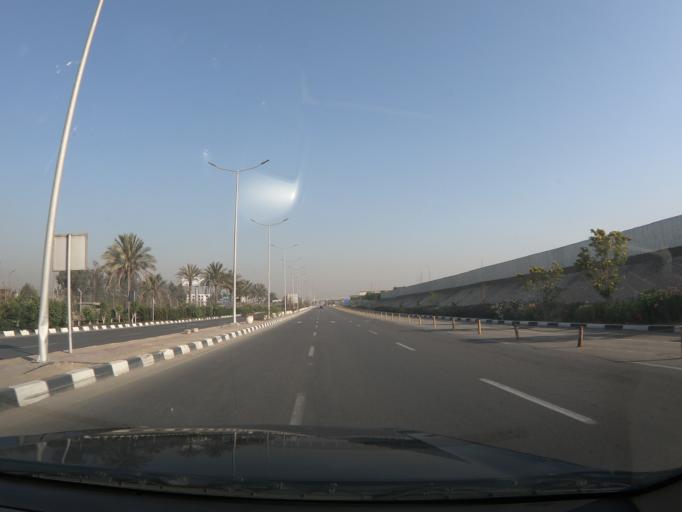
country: EG
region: Muhafazat al Qalyubiyah
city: Al Khankah
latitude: 30.1056
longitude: 31.3872
